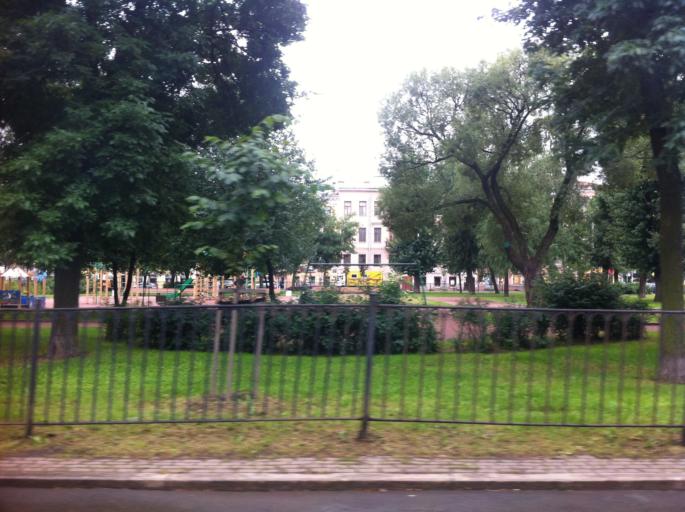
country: RU
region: St.-Petersburg
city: Admiralteisky
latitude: 59.9189
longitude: 30.2898
